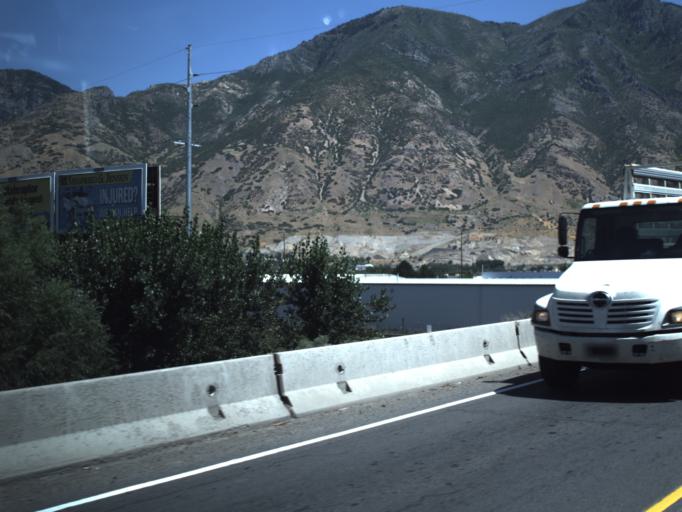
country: US
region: Utah
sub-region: Utah County
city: Springville
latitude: 40.1881
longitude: -111.6388
